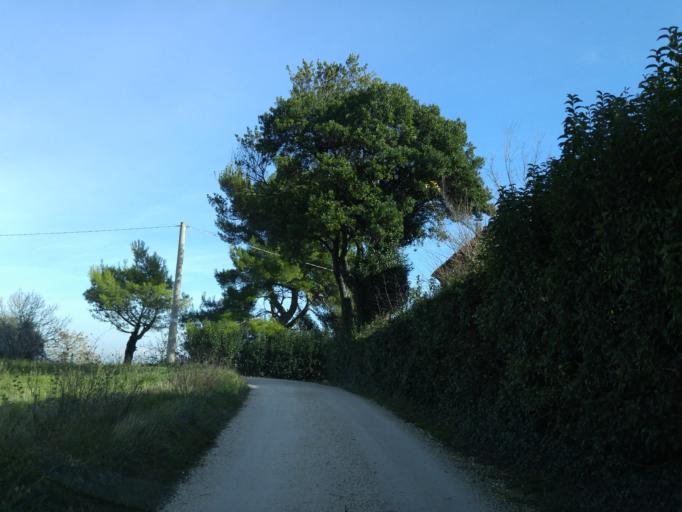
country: IT
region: The Marches
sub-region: Provincia di Pesaro e Urbino
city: Saltara
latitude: 43.7554
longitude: 12.9013
